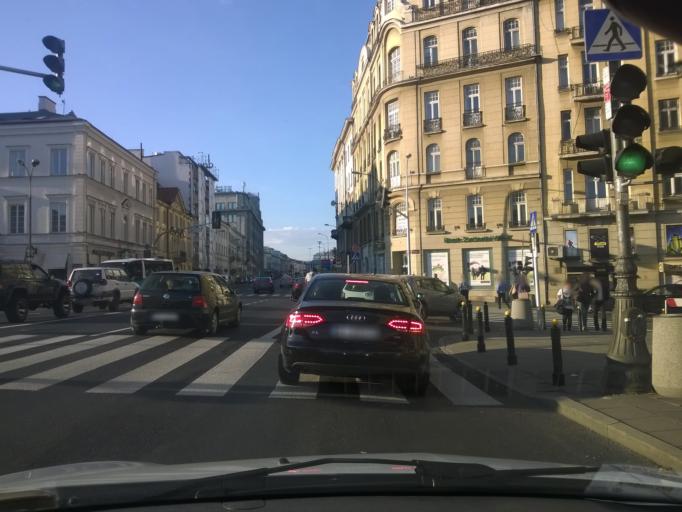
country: PL
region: Masovian Voivodeship
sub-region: Warszawa
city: Srodmiescie
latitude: 52.2296
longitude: 21.0226
